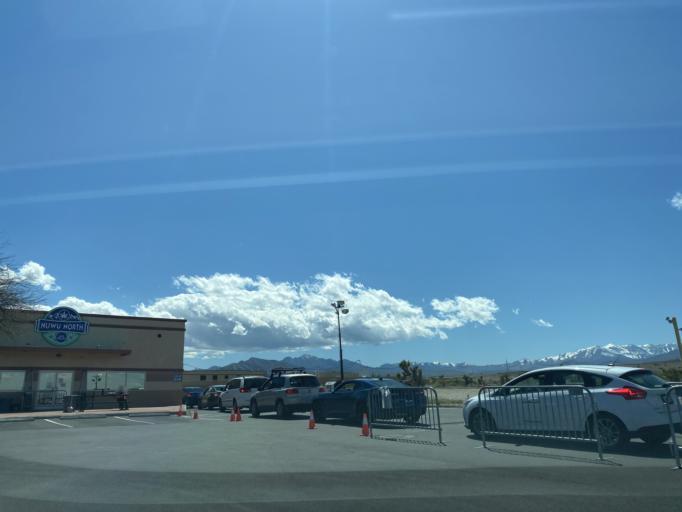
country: US
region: Nevada
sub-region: Clark County
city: Summerlin South
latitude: 36.3640
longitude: -115.3461
